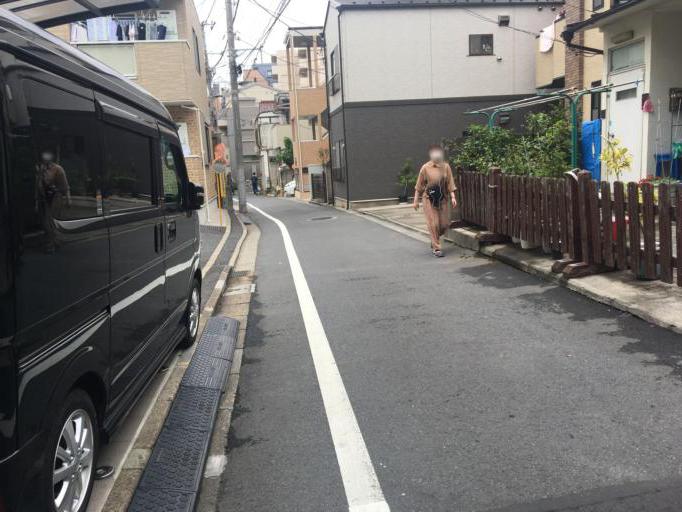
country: JP
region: Saitama
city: Soka
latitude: 35.7390
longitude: 139.7963
